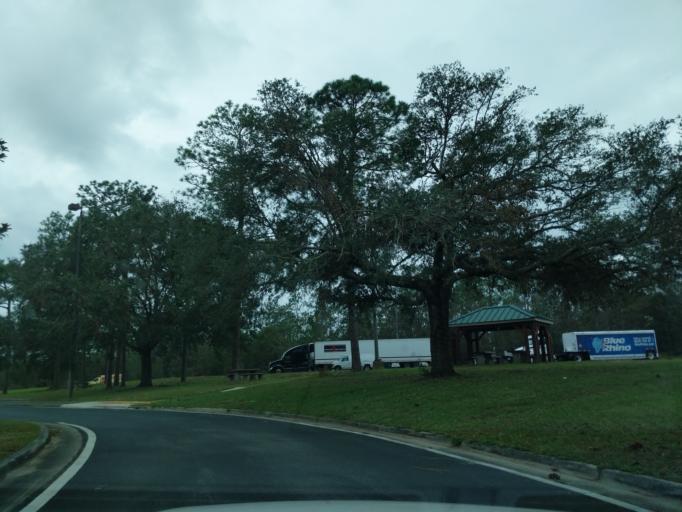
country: US
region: Florida
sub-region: Escambia County
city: Cantonment
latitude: 30.5787
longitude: -87.4221
